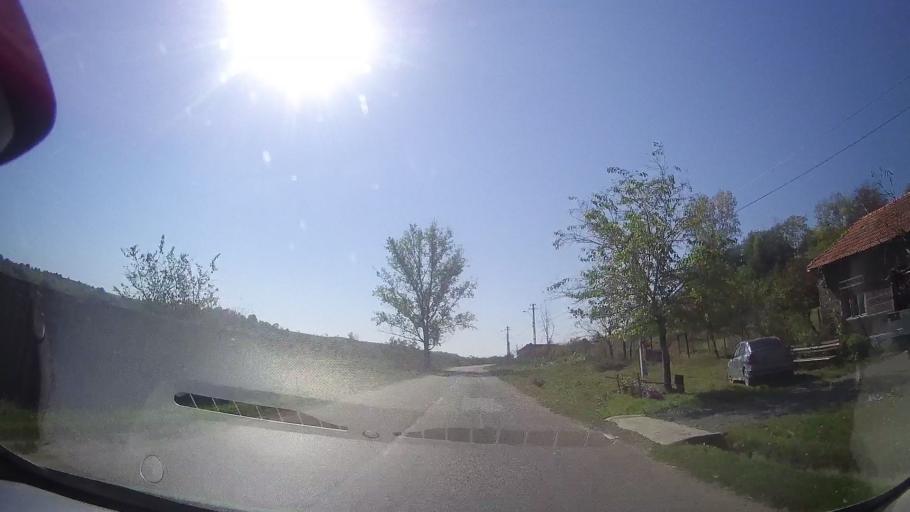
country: RO
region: Timis
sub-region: Comuna Ohaba Lunga
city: Ohaba Lunga
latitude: 45.9050
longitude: 21.9805
